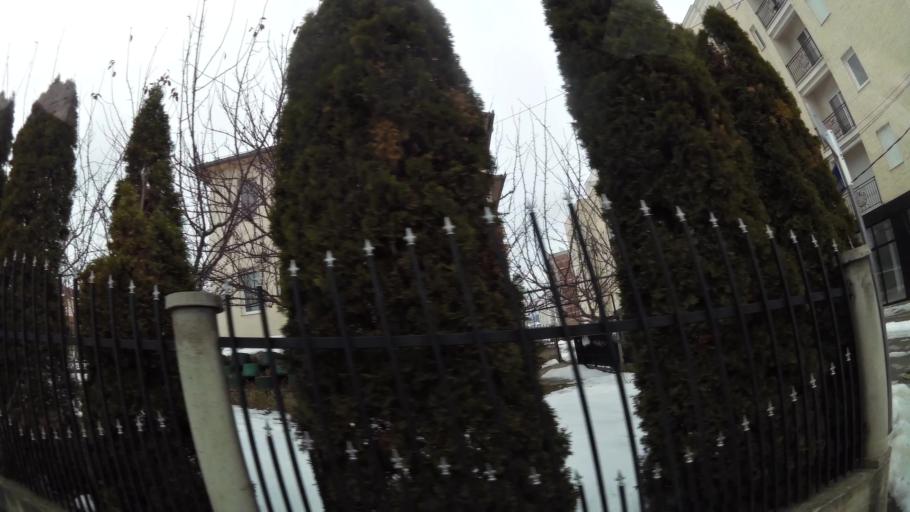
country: XK
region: Pristina
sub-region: Komuna e Prishtines
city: Pristina
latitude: 42.6436
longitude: 21.1810
